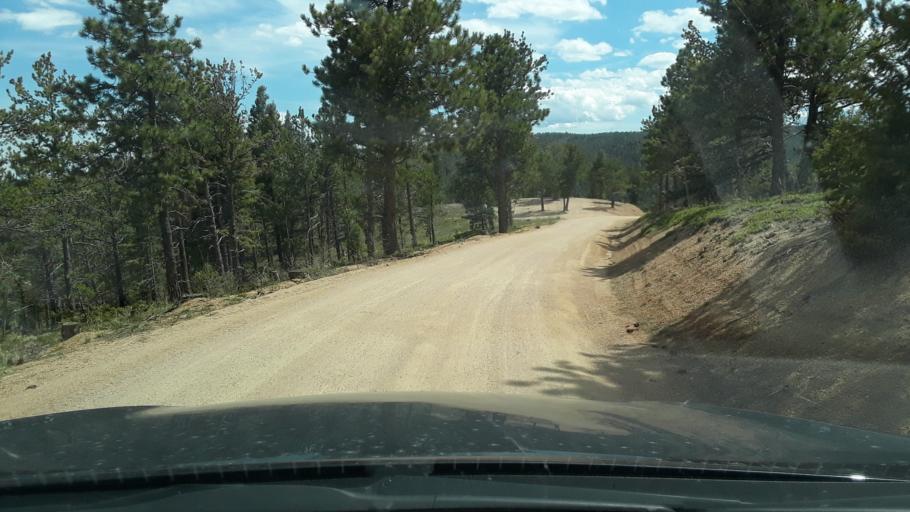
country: US
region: Colorado
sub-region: El Paso County
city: Palmer Lake
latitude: 39.0696
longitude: -104.9495
